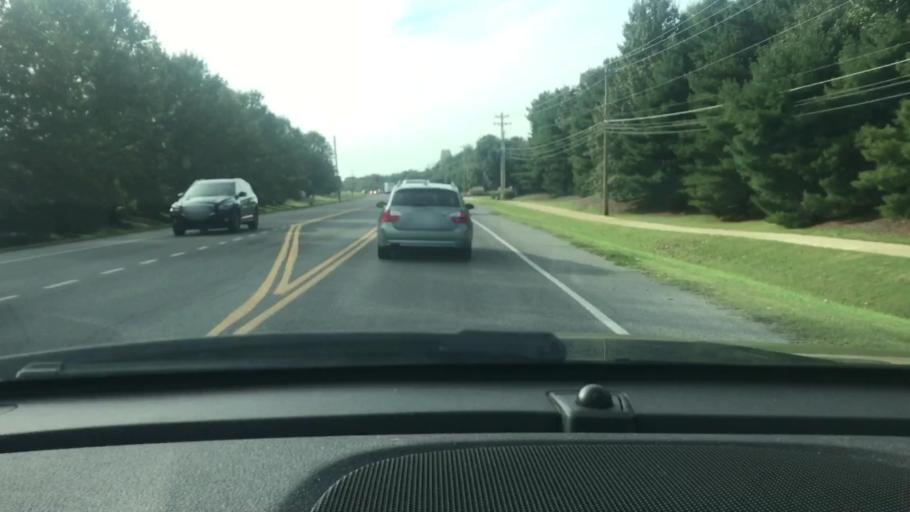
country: US
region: Tennessee
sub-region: Williamson County
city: Franklin
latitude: 35.9294
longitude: -86.8942
